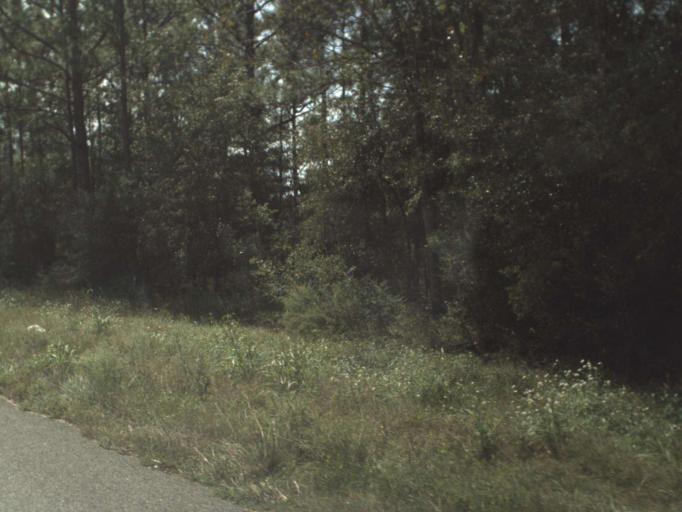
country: US
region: Florida
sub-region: Washington County
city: Chipley
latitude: 30.5885
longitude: -85.5919
